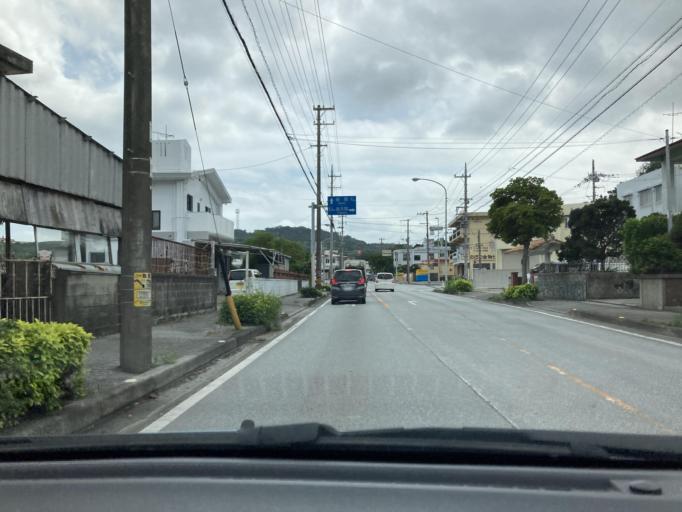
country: JP
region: Okinawa
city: Chatan
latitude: 26.2836
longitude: 127.7848
